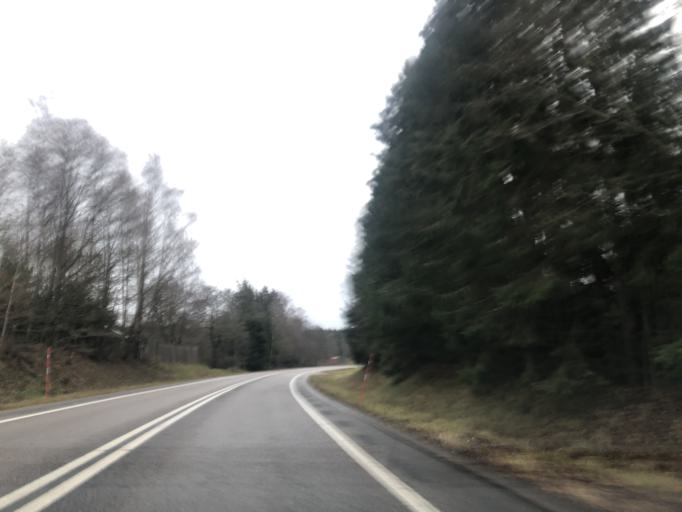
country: SE
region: Vaestra Goetaland
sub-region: Ulricehamns Kommun
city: Ulricehamn
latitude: 57.8125
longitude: 13.2932
